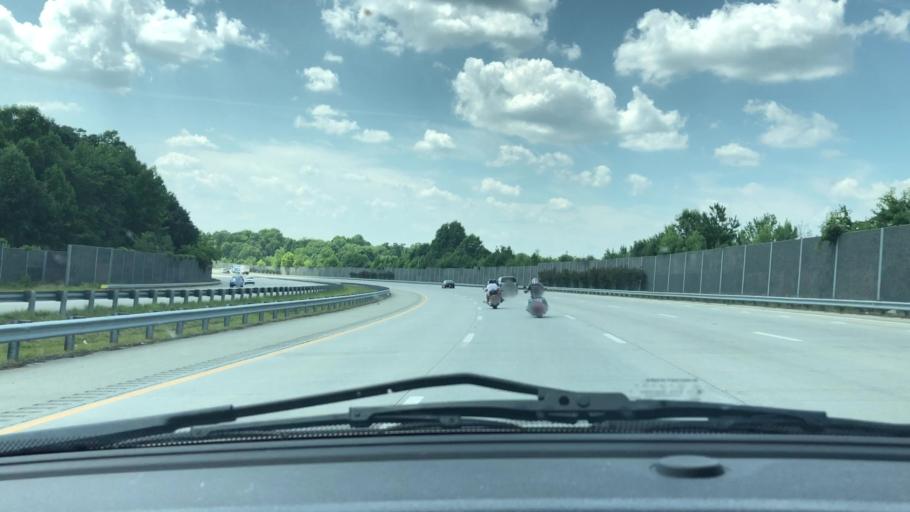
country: US
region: North Carolina
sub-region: Guilford County
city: Greensboro
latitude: 36.0189
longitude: -79.8541
